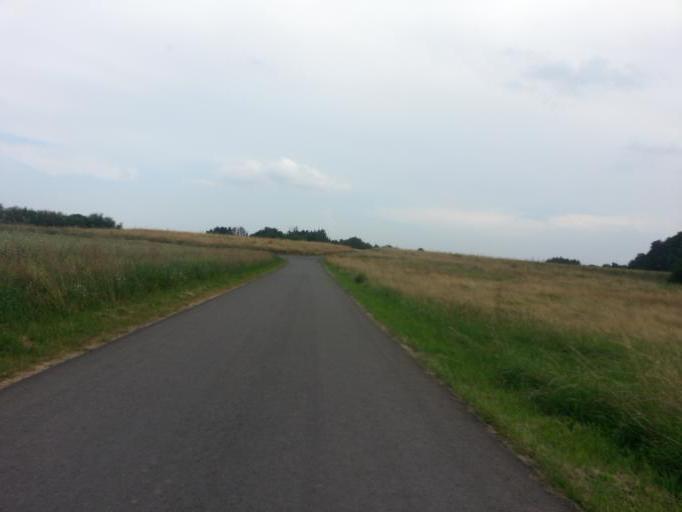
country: DE
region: Saarland
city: Oberthal
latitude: 49.5405
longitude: 7.1042
